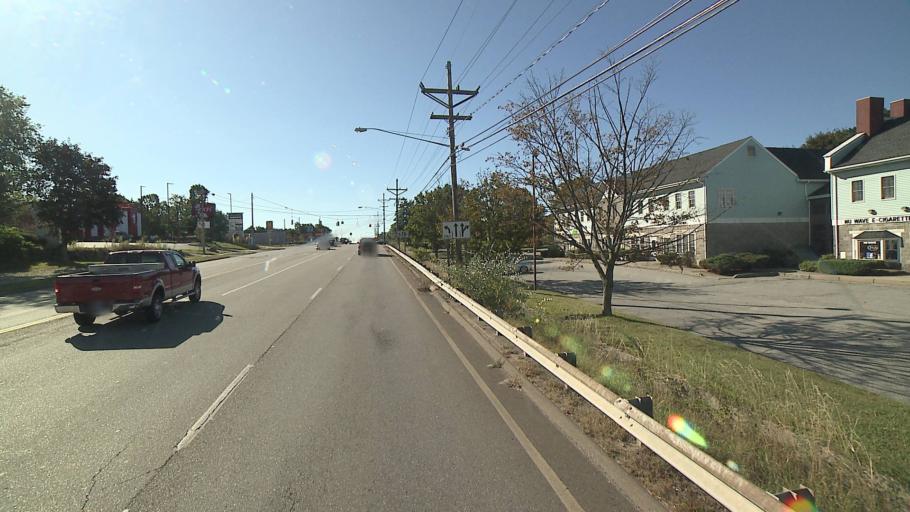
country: US
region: Connecticut
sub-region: New London County
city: Conning Towers-Nautilus Park
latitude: 41.3694
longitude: -72.0709
